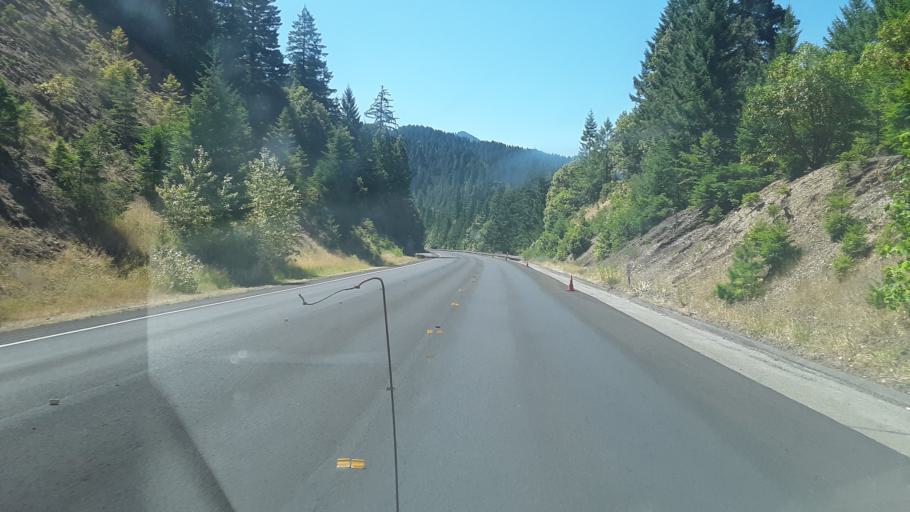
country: US
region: Oregon
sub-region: Josephine County
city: Cave Junction
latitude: 41.9615
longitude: -123.7464
